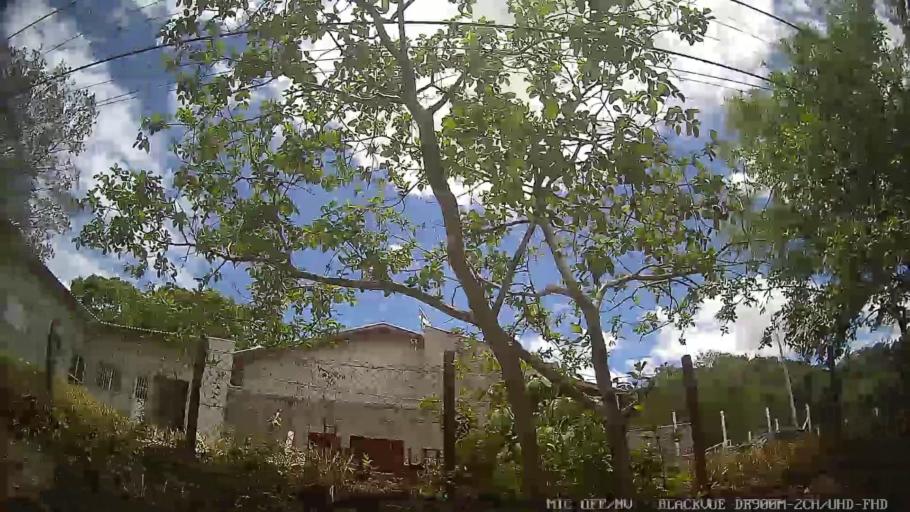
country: BR
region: Sao Paulo
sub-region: Jaguariuna
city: Jaguariuna
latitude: -22.7111
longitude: -46.9716
